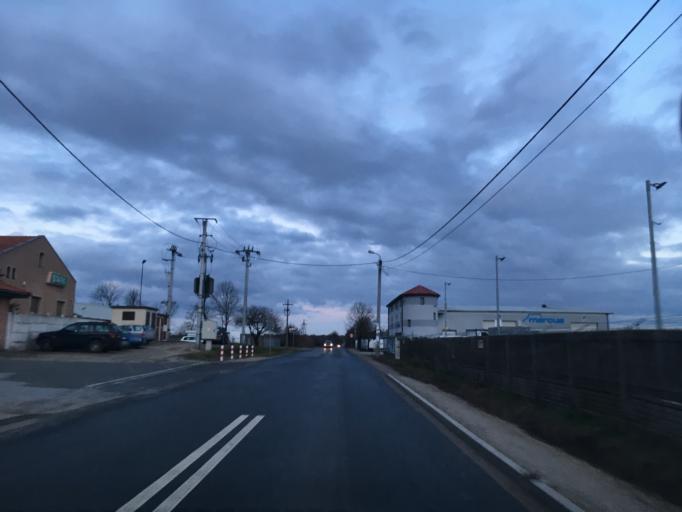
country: PL
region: Masovian Voivodeship
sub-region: Powiat pruszkowski
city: Owczarnia
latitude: 52.0814
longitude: 20.7209
